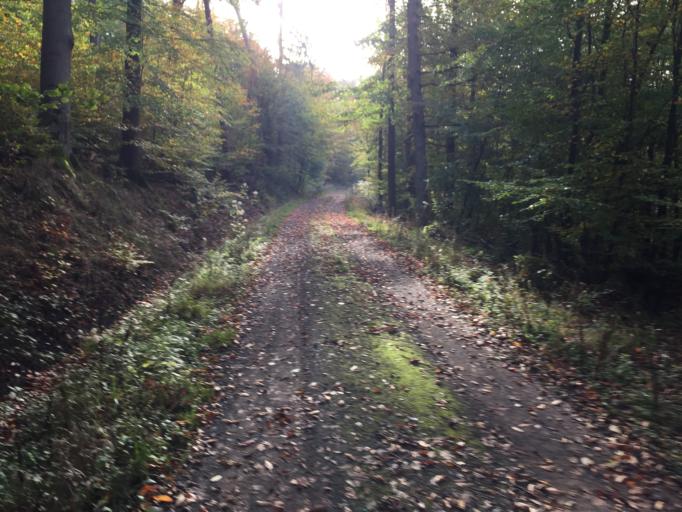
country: DE
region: Hesse
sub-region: Regierungsbezirk Giessen
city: Laubach
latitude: 50.5717
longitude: 8.9944
